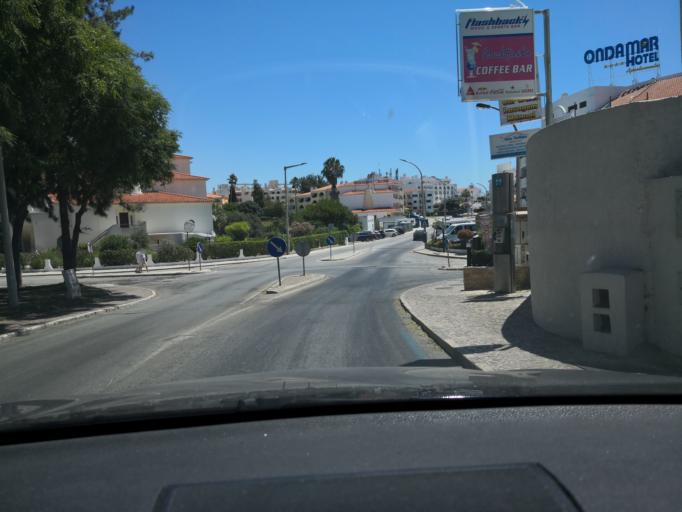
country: PT
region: Faro
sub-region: Albufeira
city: Albufeira
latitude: 37.0924
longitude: -8.2363
